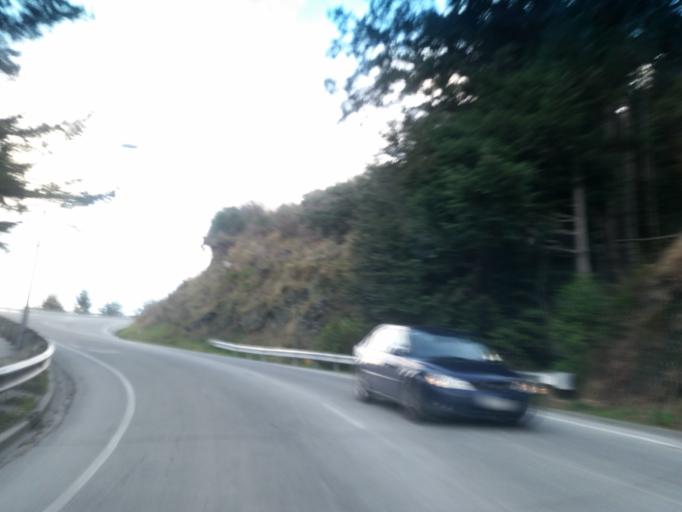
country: NZ
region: Otago
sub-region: Queenstown-Lakes District
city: Queenstown
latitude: -45.0371
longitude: 168.6412
